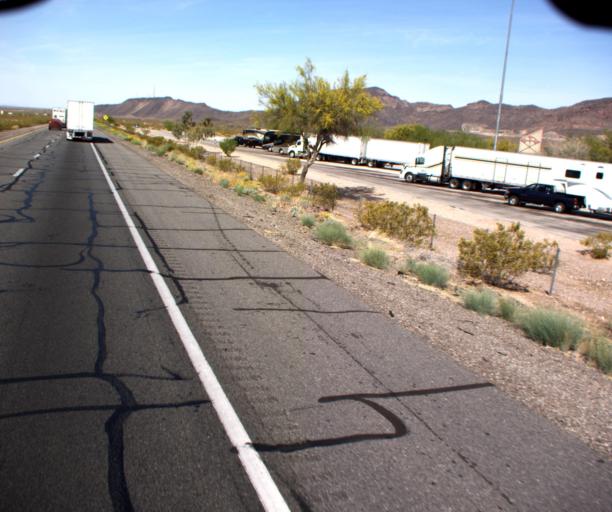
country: US
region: Arizona
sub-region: Maricopa County
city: Buckeye
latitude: 33.5204
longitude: -113.0667
